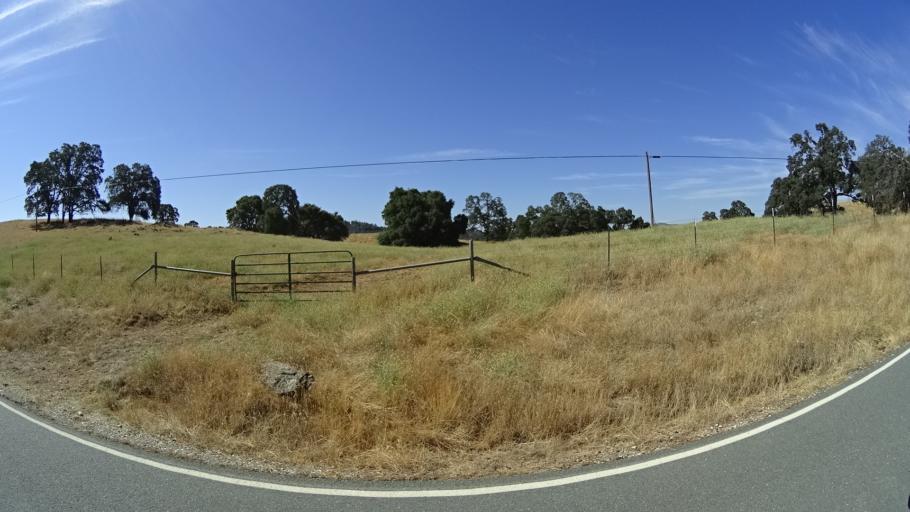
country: US
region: California
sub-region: Calaveras County
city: San Andreas
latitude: 38.1483
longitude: -120.6055
